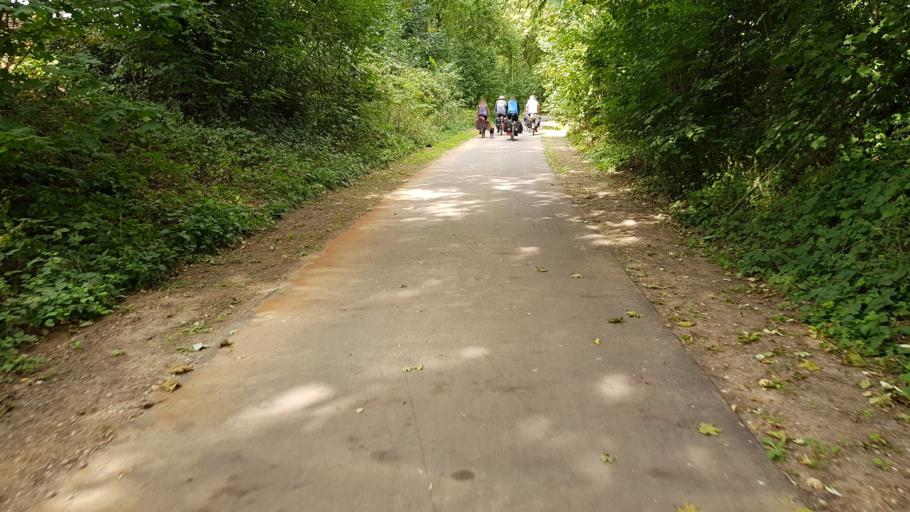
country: PL
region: West Pomeranian Voivodeship
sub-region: Powiat pyrzycki
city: Pyrzyce
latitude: 53.1332
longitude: 14.9794
